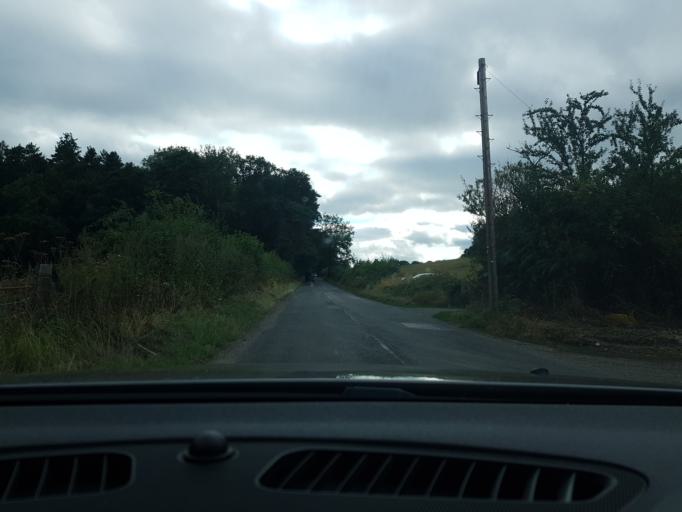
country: GB
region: England
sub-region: West Berkshire
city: Hermitage
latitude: 51.4596
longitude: -1.2551
